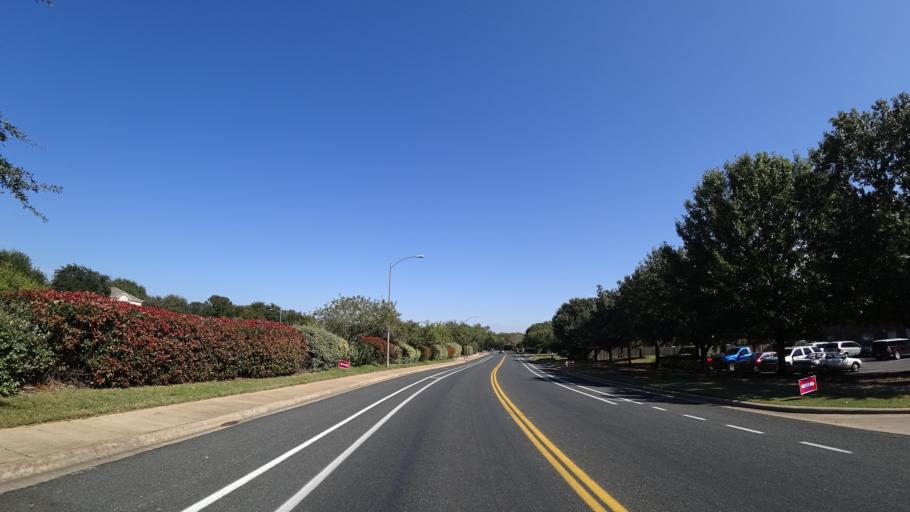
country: US
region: Texas
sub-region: Travis County
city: Shady Hollow
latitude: 30.2183
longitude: -97.8608
